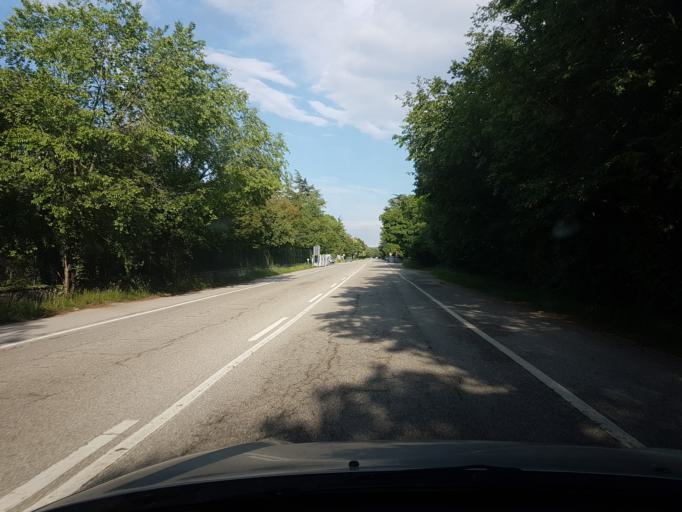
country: IT
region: Friuli Venezia Giulia
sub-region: Provincia di Trieste
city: Villa Opicina
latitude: 45.6815
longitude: 13.7948
